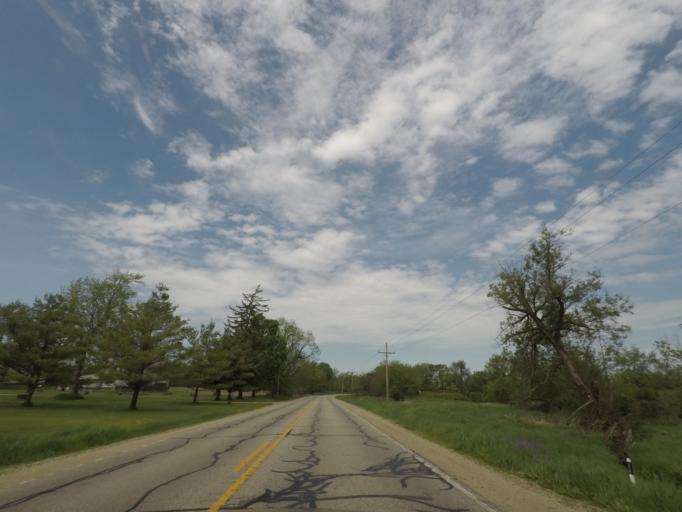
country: US
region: Wisconsin
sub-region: Rock County
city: Orfordville
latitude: 42.6109
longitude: -89.2337
